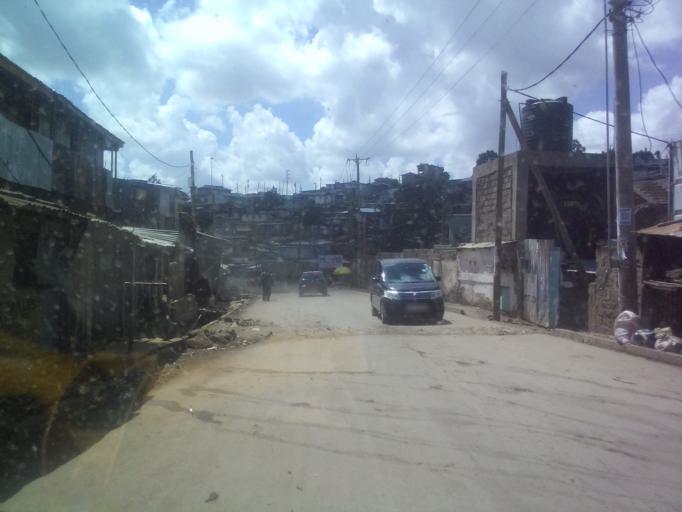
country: KE
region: Nairobi Area
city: Nairobi
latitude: -1.3158
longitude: 36.7755
